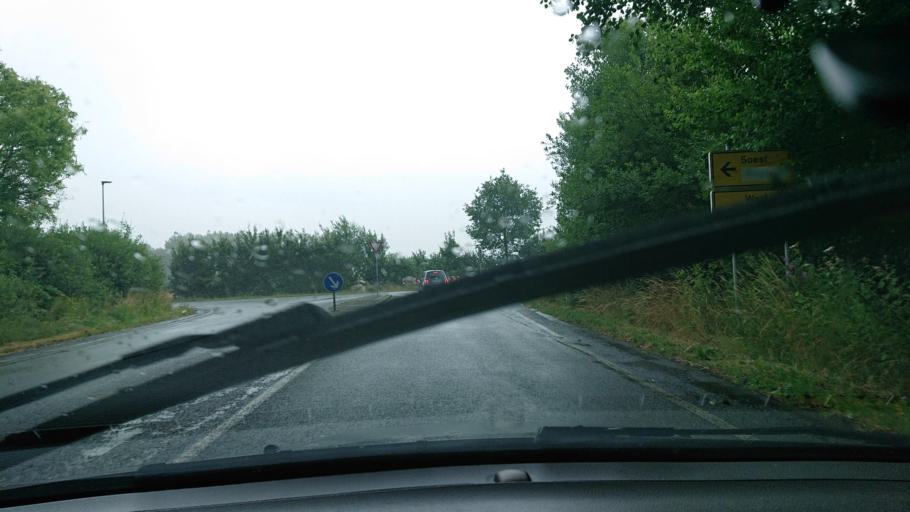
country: DE
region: North Rhine-Westphalia
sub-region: Regierungsbezirk Arnsberg
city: Hamm
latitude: 51.6682
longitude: 7.8907
